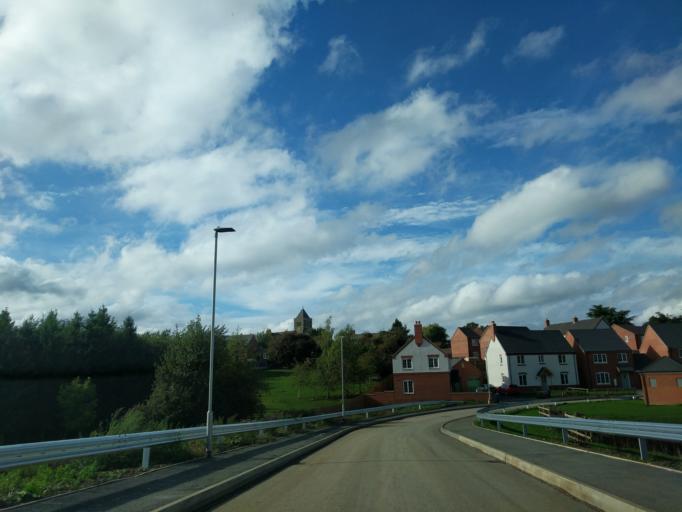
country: GB
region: England
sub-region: Leicestershire
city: Coalville
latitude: 52.7089
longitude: -1.3659
